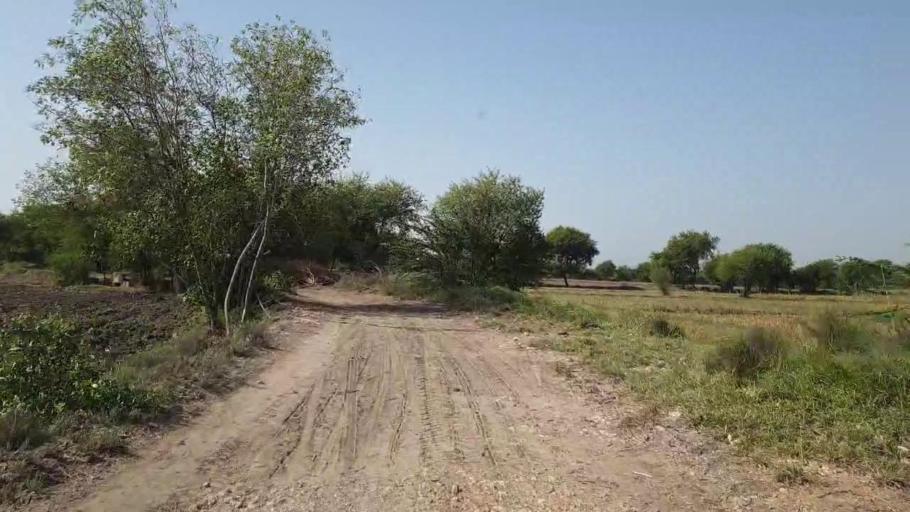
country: PK
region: Sindh
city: Kadhan
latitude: 24.6181
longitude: 69.0719
